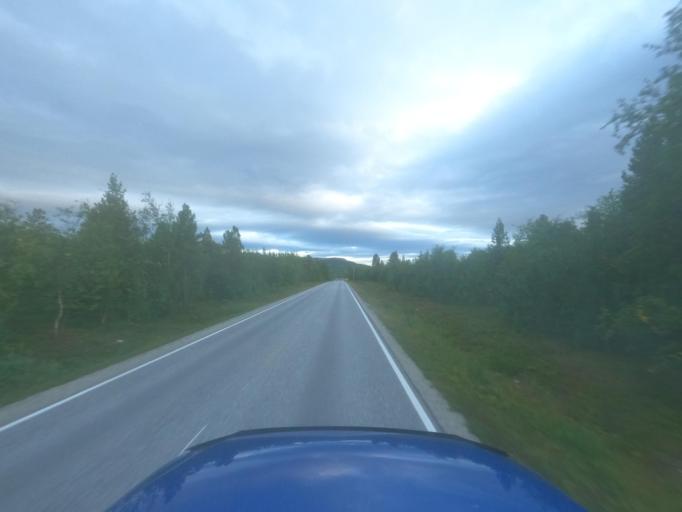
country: NO
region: Finnmark Fylke
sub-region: Porsanger
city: Lakselv
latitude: 69.9811
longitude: 24.9601
